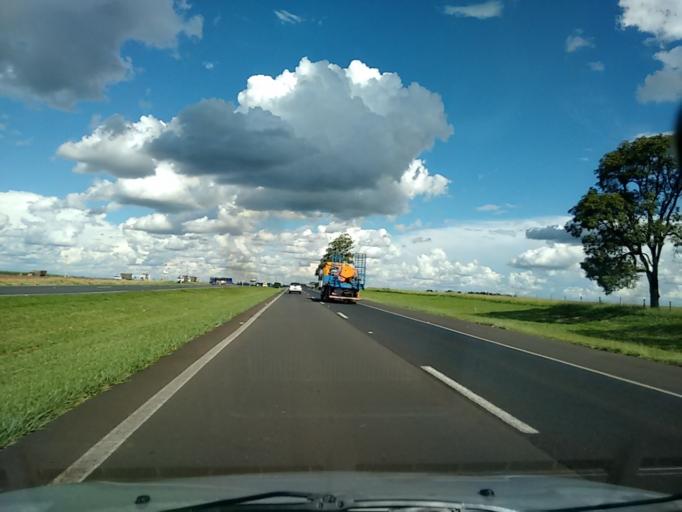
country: BR
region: Sao Paulo
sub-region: Ibate
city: Ibate
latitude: -21.8998
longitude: -48.0633
